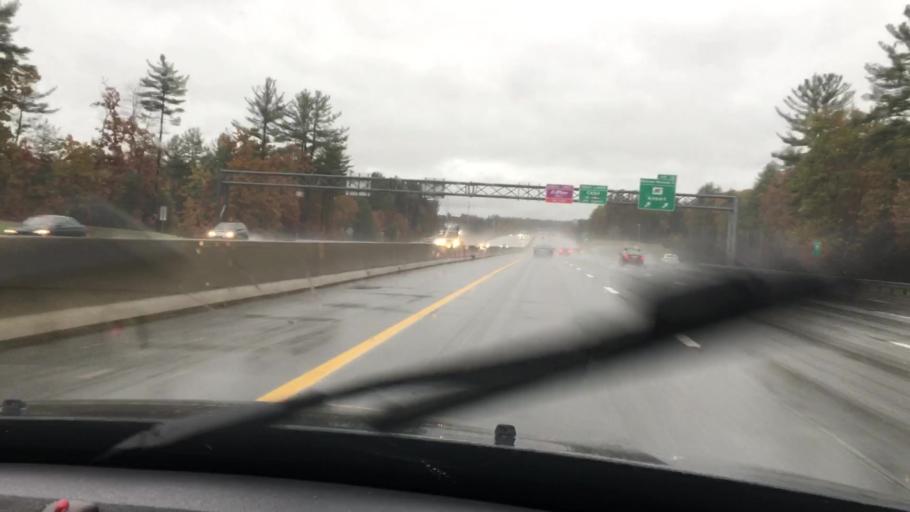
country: US
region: New Hampshire
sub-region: Hillsborough County
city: Bedford
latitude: 42.9238
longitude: -71.4668
